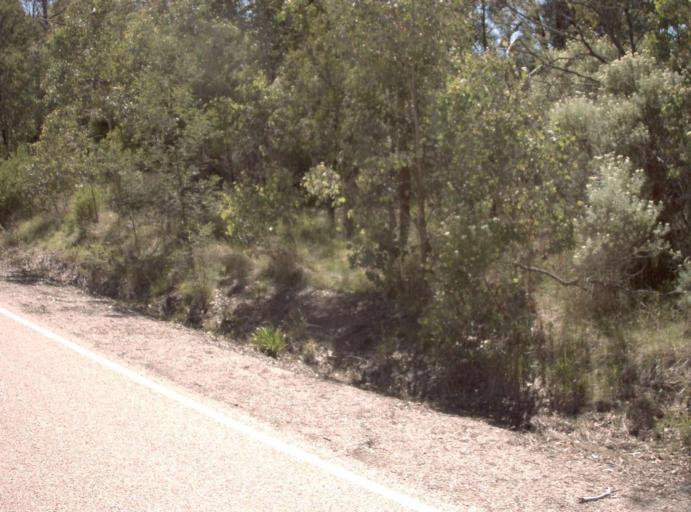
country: AU
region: Victoria
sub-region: East Gippsland
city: Lakes Entrance
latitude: -37.3317
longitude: 148.2336
